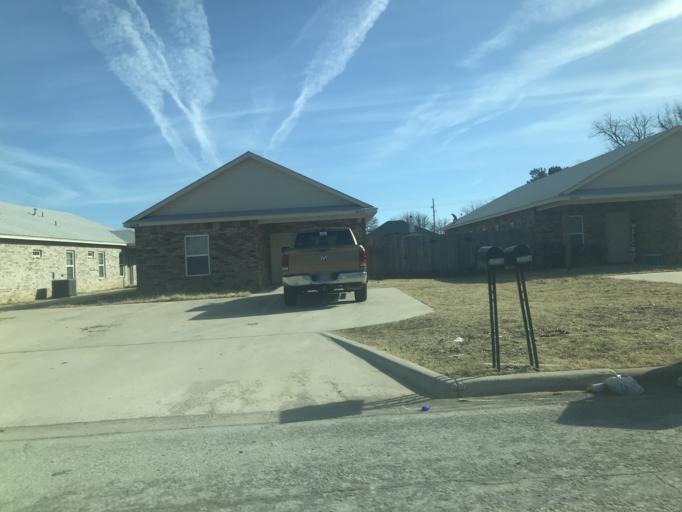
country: US
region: Texas
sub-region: Taylor County
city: Abilene
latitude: 32.4876
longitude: -99.7361
